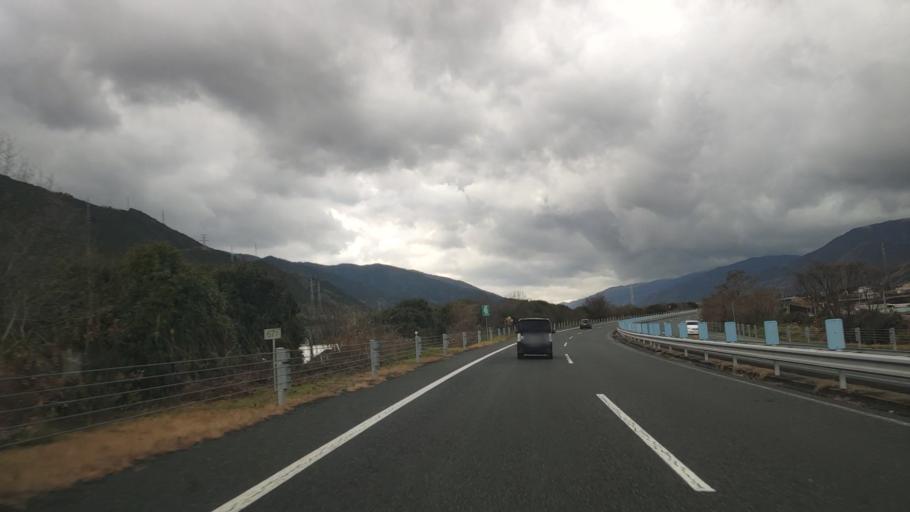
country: JP
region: Tokushima
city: Ikedacho
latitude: 34.0368
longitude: 133.9029
